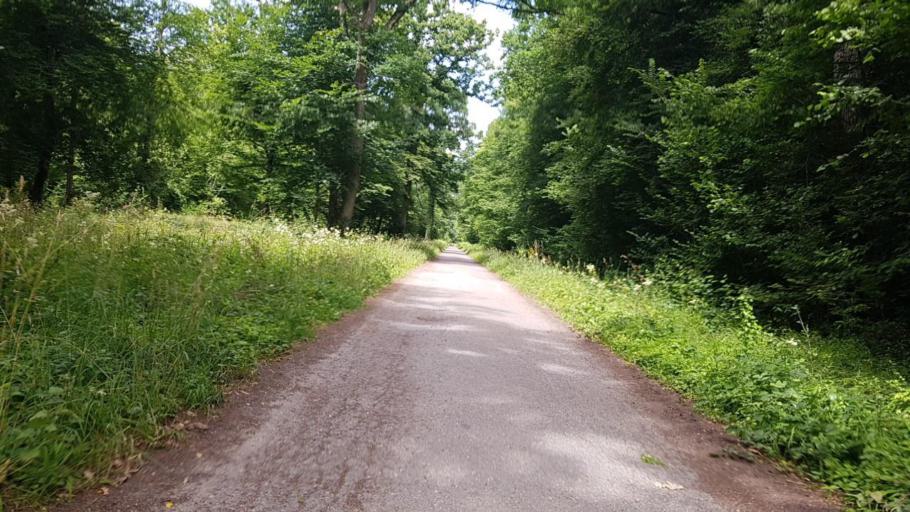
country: FR
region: Picardie
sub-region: Departement de l'Oise
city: Montmacq
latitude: 49.4723
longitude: 2.9189
